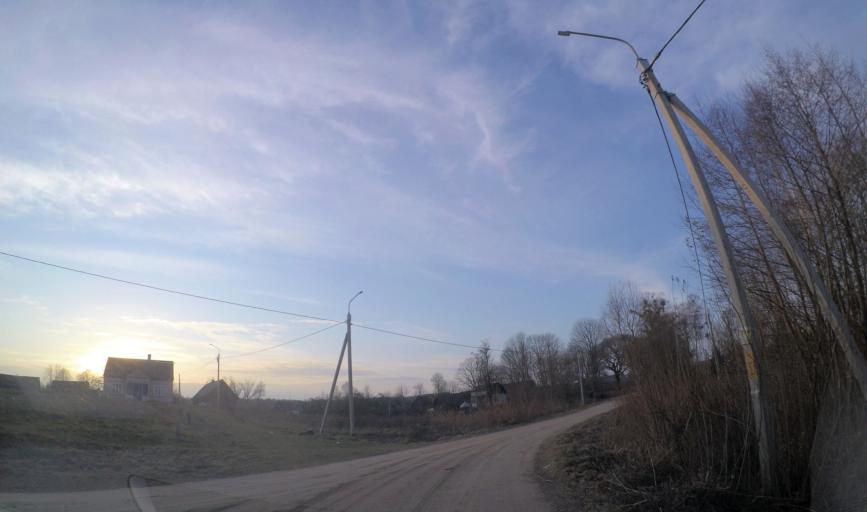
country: LT
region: Alytaus apskritis
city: Druskininkai
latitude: 53.9106
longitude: 24.1802
